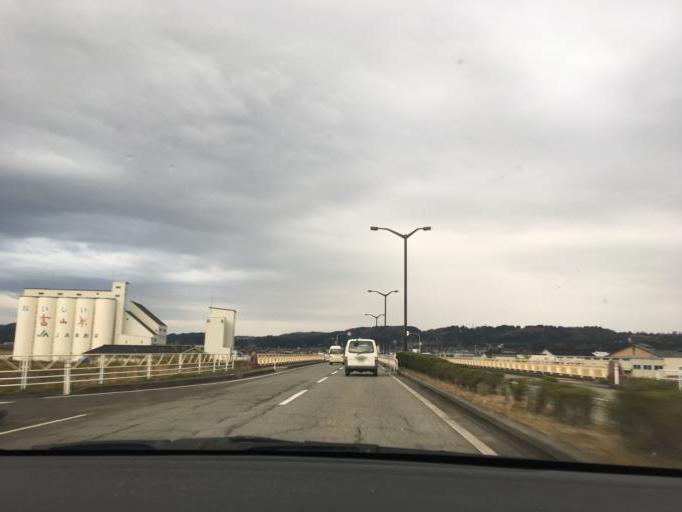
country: JP
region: Toyama
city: Toyama-shi
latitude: 36.6581
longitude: 137.1461
